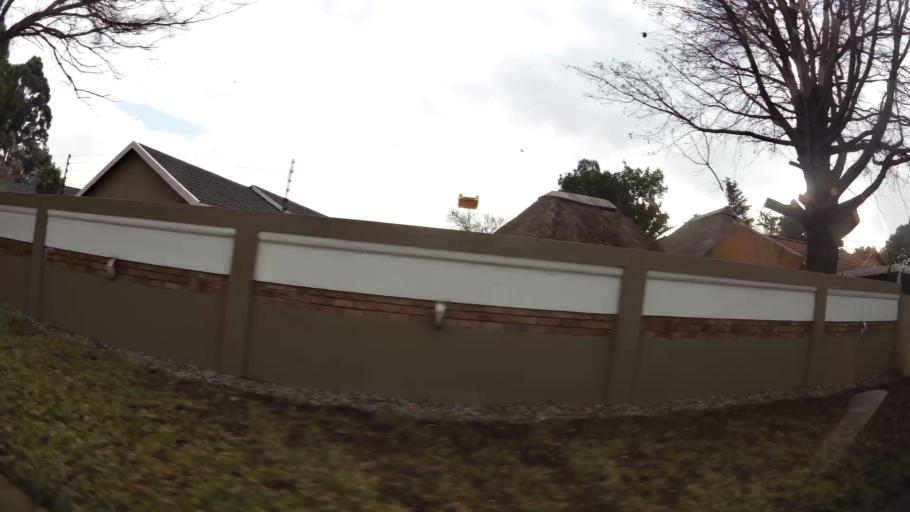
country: ZA
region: Gauteng
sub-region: Ekurhuleni Metropolitan Municipality
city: Benoni
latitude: -26.1341
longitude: 28.3597
